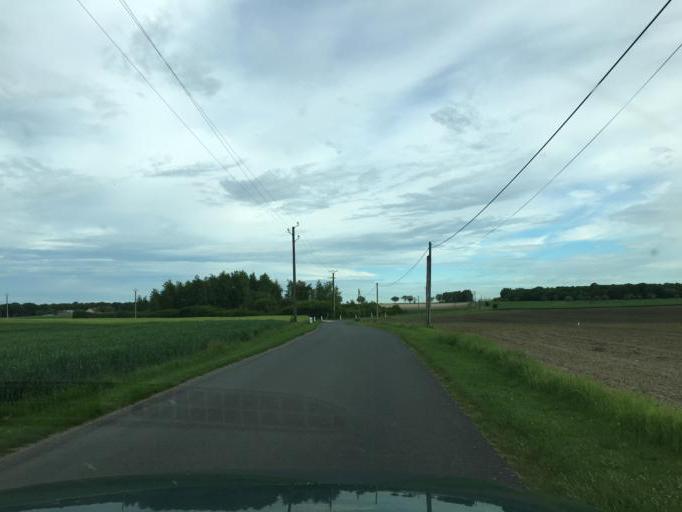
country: FR
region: Centre
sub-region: Departement du Loiret
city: Ormes
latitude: 47.9415
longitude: 1.7599
